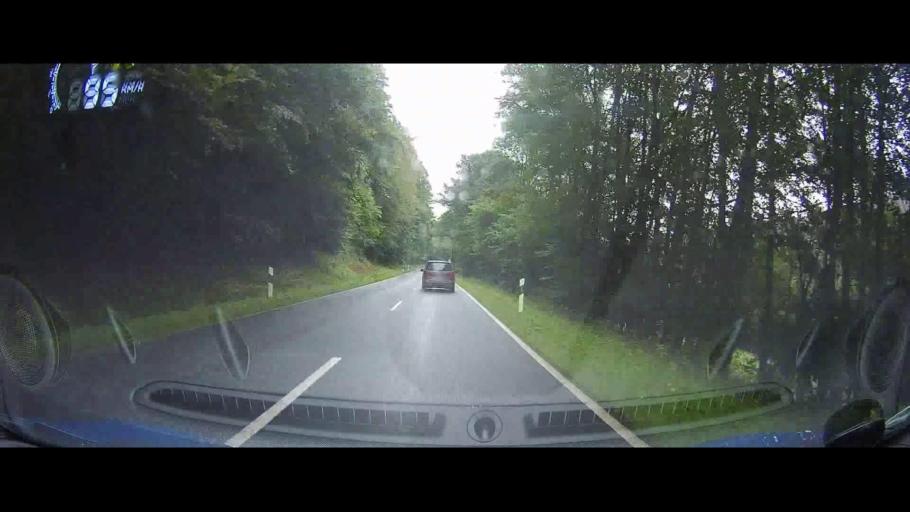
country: DE
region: Lower Saxony
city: Uslar
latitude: 51.7069
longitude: 9.6233
